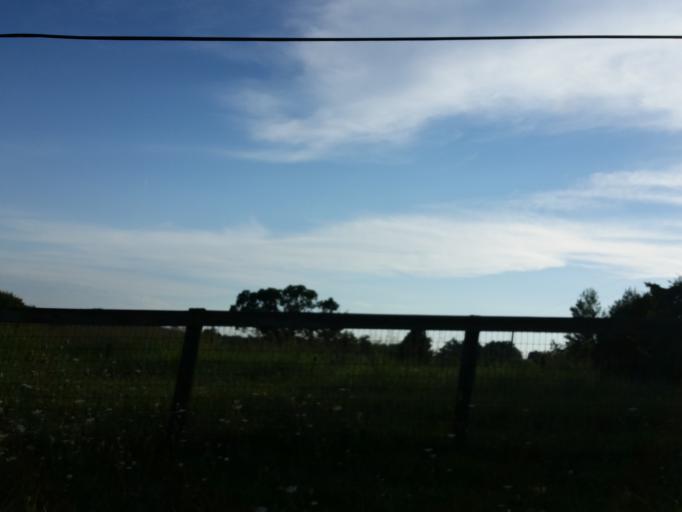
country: US
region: Tennessee
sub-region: Blount County
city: Eagleton Village
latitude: 35.8750
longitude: -83.9269
